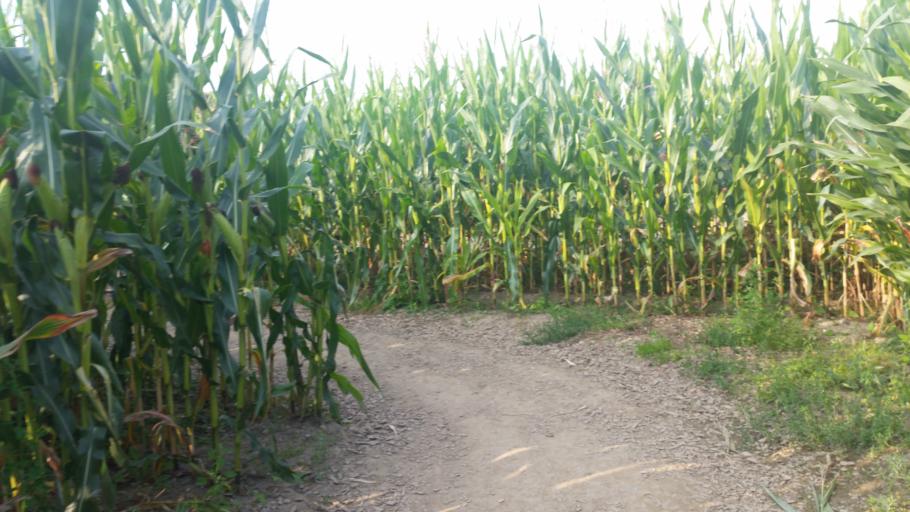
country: BE
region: Wallonia
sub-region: Province du Luxembourg
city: Durbuy
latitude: 50.3577
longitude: 5.5018
